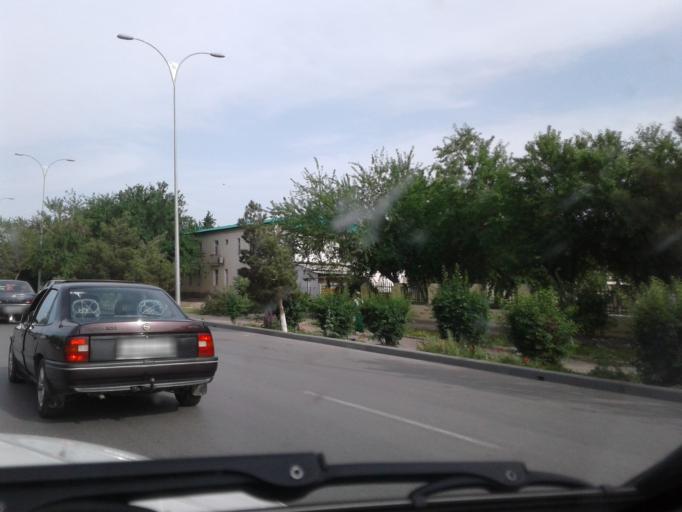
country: TM
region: Mary
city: Mary
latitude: 37.5905
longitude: 61.8315
